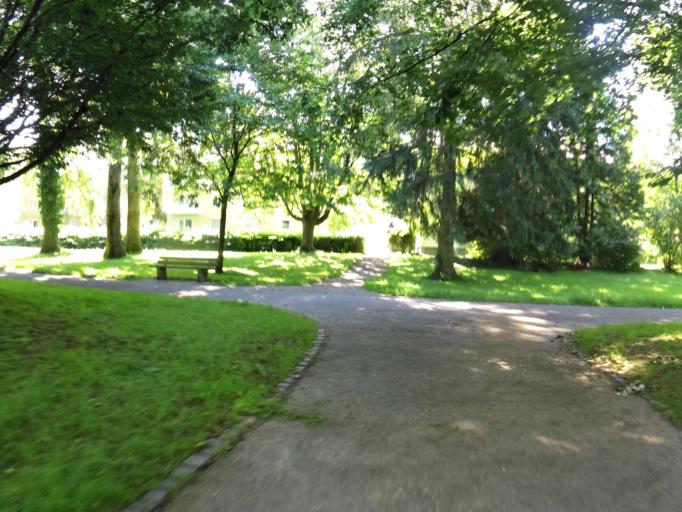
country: DE
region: Baden-Wuerttemberg
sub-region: Freiburg Region
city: Lahr
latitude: 48.3325
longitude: 7.8740
